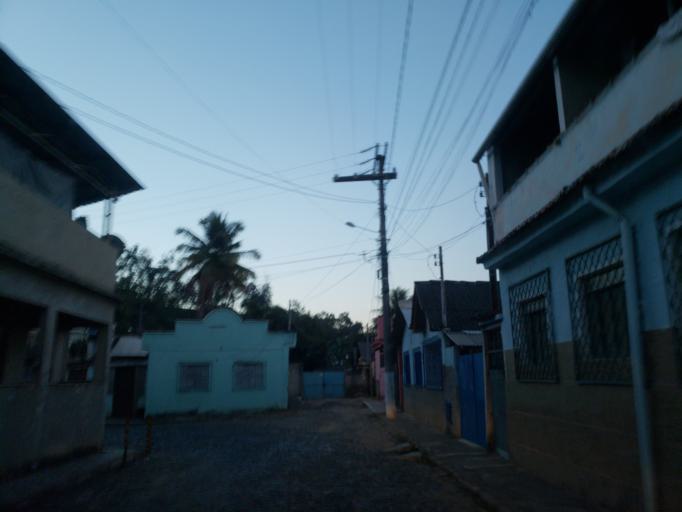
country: BR
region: Minas Gerais
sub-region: Sao Joao Nepomuceno
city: Sao Joao Nepomuceno
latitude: -21.5259
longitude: -43.0146
